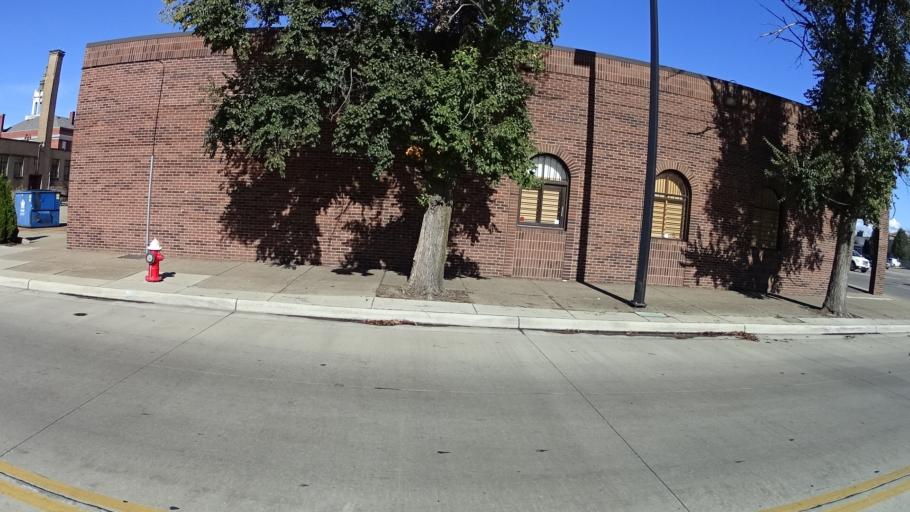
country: US
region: Ohio
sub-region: Lorain County
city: Lorain
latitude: 41.4657
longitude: -82.1789
